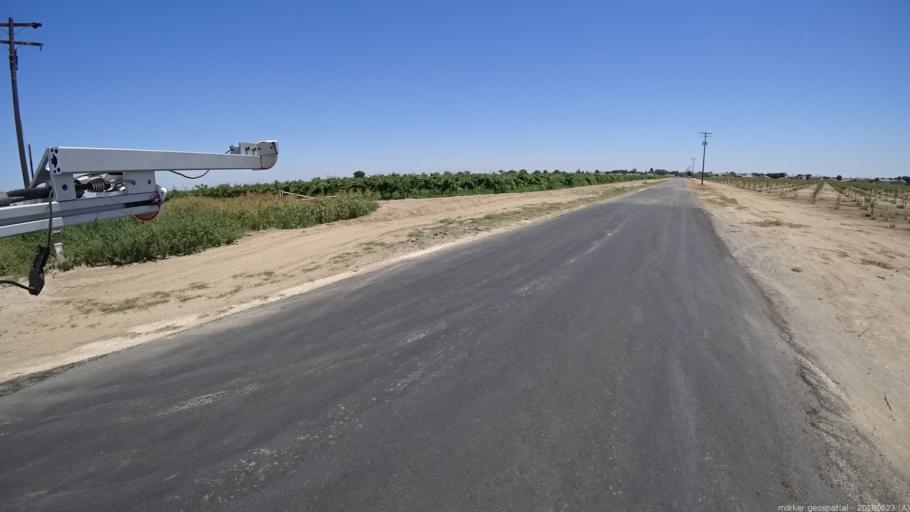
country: US
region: California
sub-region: Madera County
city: Chowchilla
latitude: 37.1200
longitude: -120.2927
